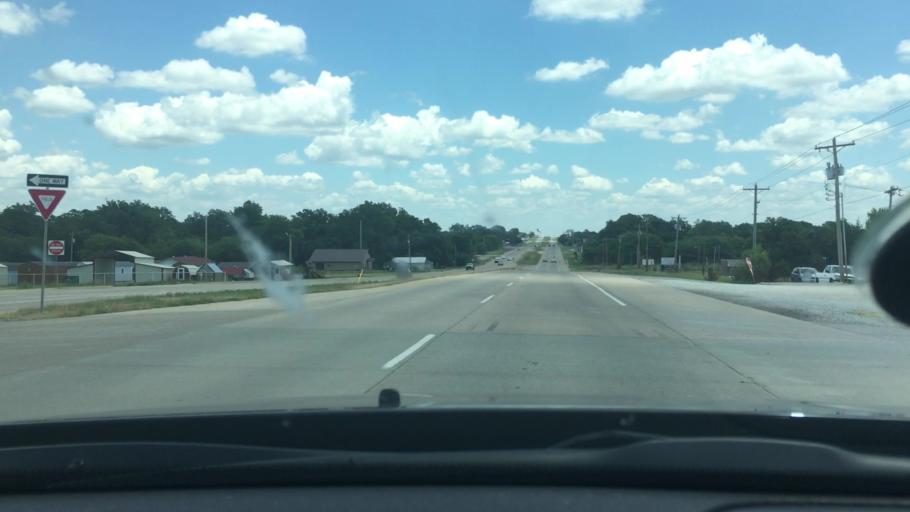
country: US
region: Oklahoma
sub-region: Carter County
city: Lone Grove
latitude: 34.1728
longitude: -97.2392
